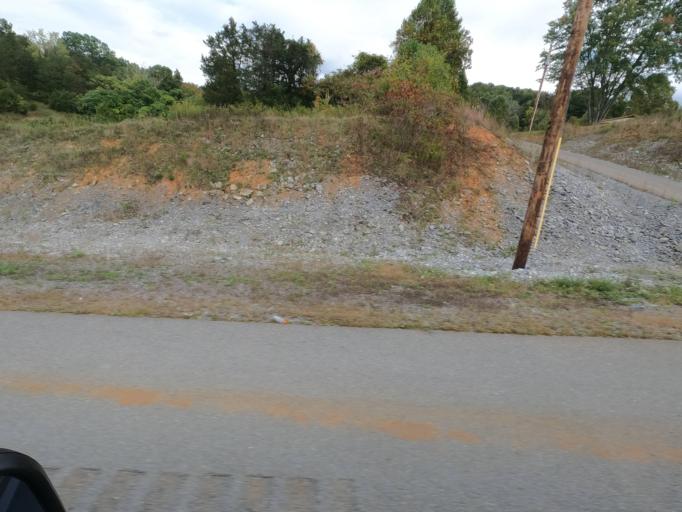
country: US
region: Tennessee
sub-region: Carter County
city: Central
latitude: 36.2872
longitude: -82.2455
